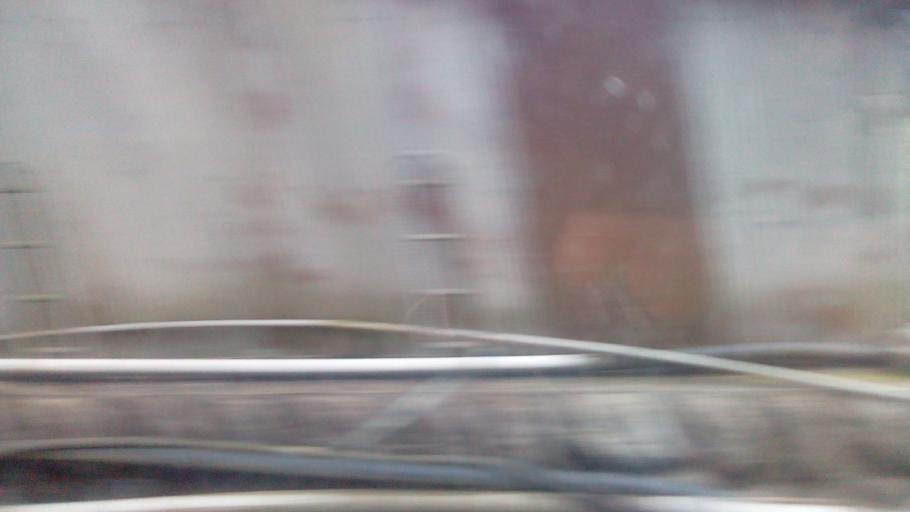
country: TW
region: Taiwan
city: Daxi
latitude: 24.4708
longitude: 121.4087
